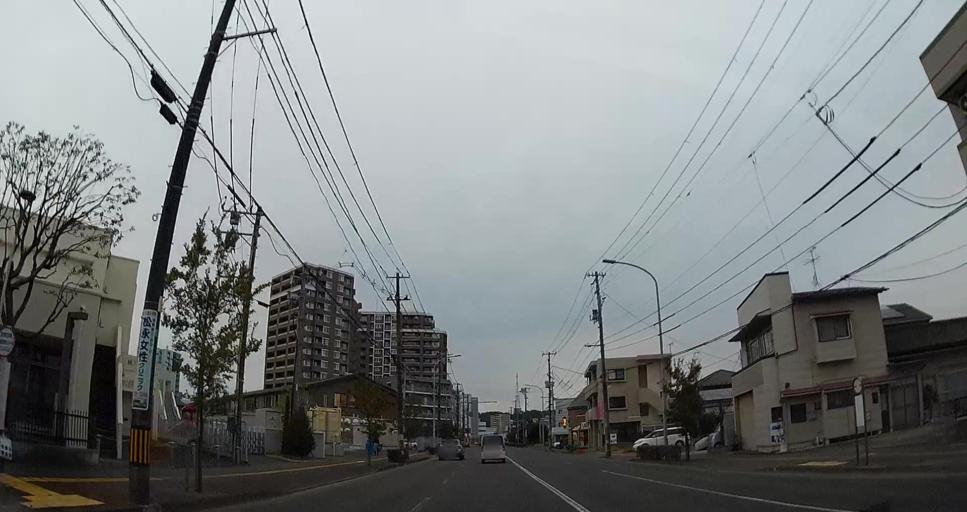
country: JP
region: Miyagi
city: Sendai
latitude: 38.2292
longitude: 140.8934
